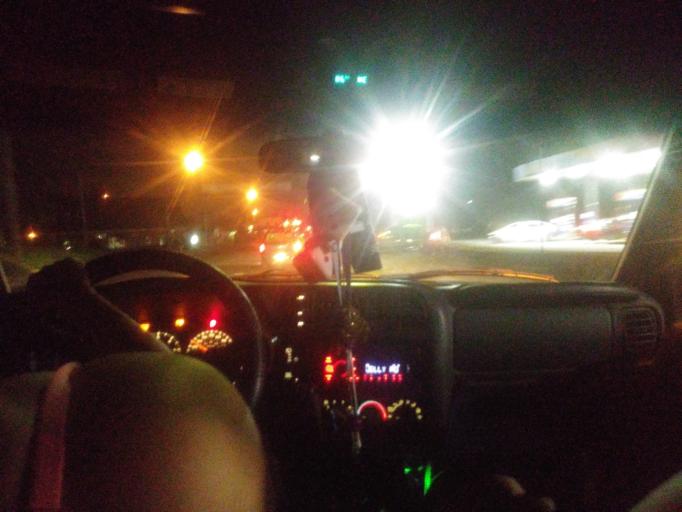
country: US
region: Ohio
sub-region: Summit County
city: Barberton
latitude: 41.0338
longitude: -81.5813
